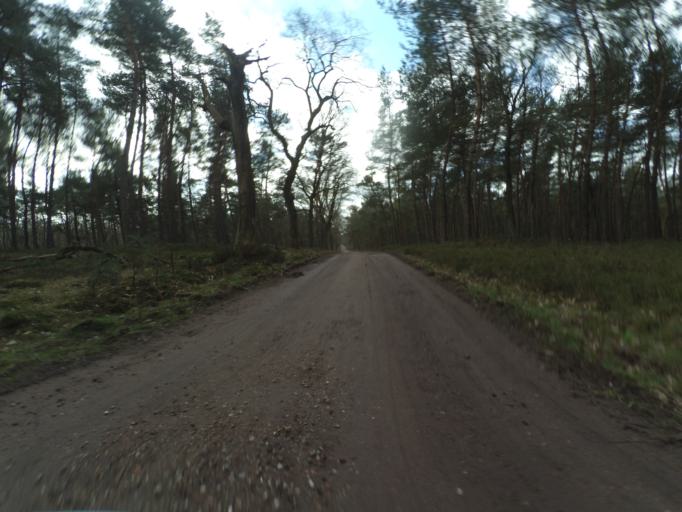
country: NL
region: Gelderland
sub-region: Gemeente Apeldoorn
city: Beekbergen
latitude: 52.0875
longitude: 5.9444
